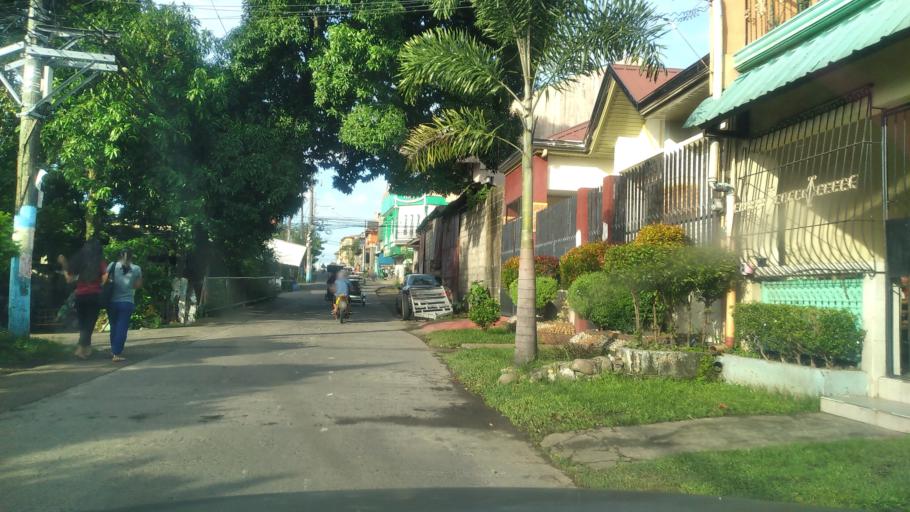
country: PH
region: Calabarzon
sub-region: Province of Quezon
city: Sariaya
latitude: 13.9644
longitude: 121.5302
